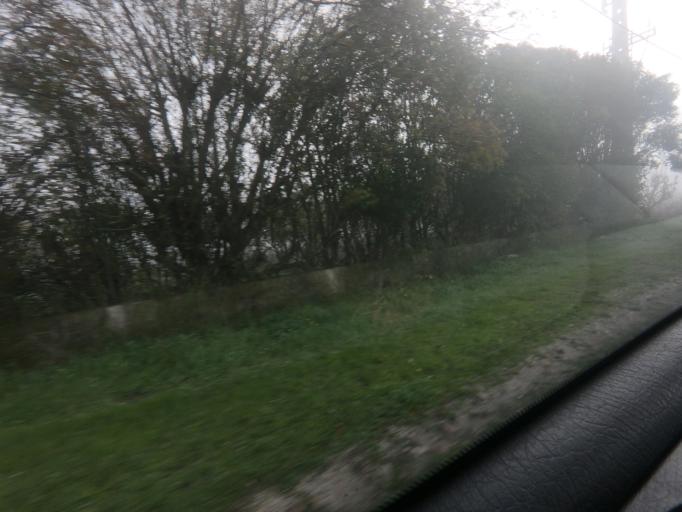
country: PT
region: Setubal
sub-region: Palmela
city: Palmela
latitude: 38.5925
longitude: -8.8401
